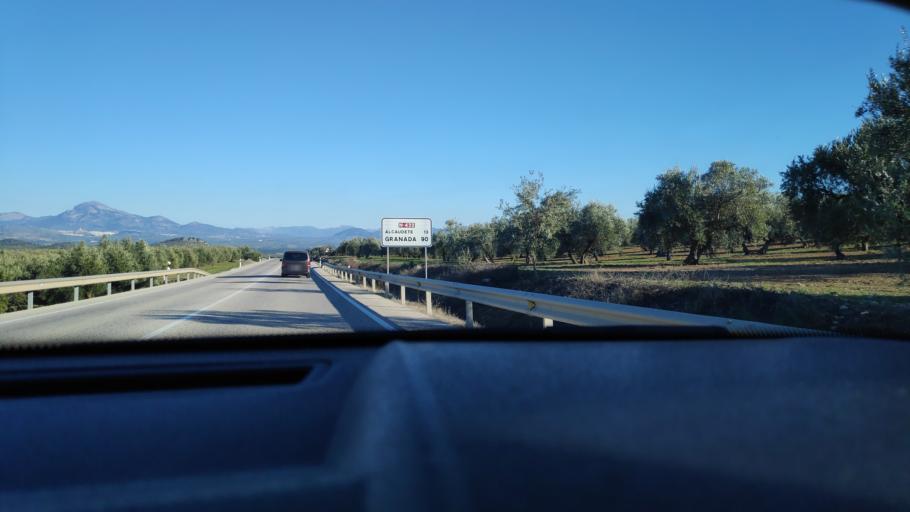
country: ES
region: Andalusia
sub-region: Province of Cordoba
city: Luque
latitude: 37.5636
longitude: -4.2098
